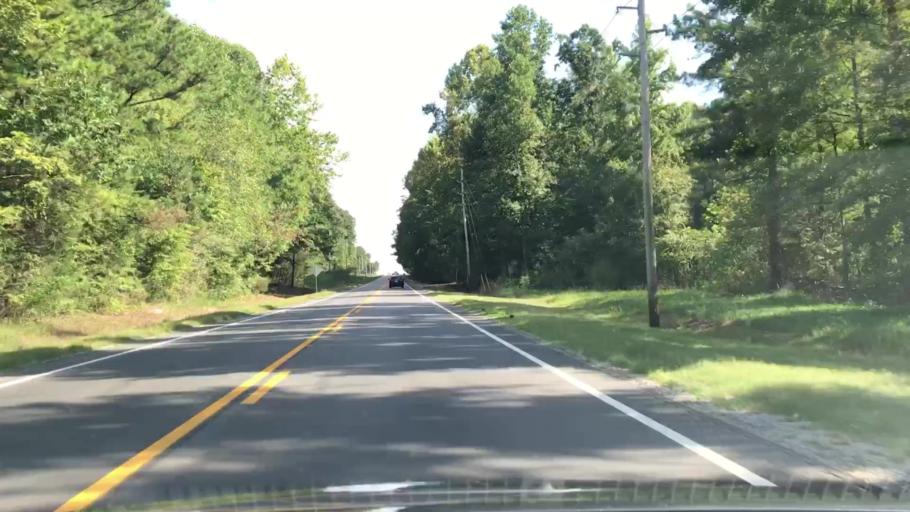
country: US
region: Alabama
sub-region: Madison County
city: Harvest
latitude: 34.9189
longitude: -86.7637
